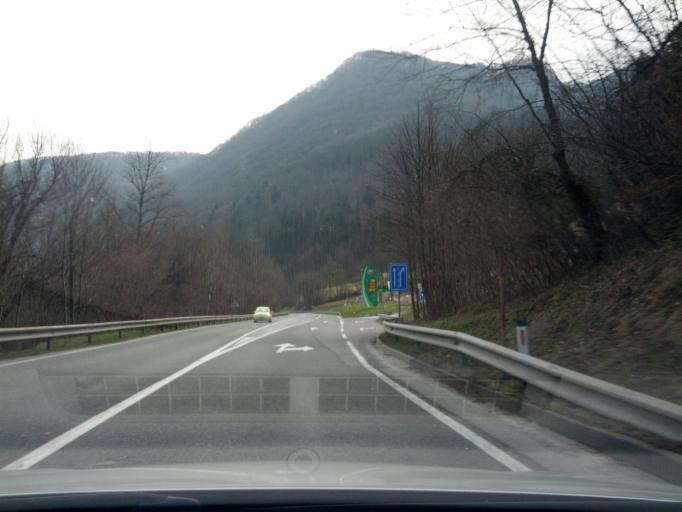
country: SI
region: Zagorje ob Savi
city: Zagorje ob Savi
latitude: 46.1112
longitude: 15.0047
